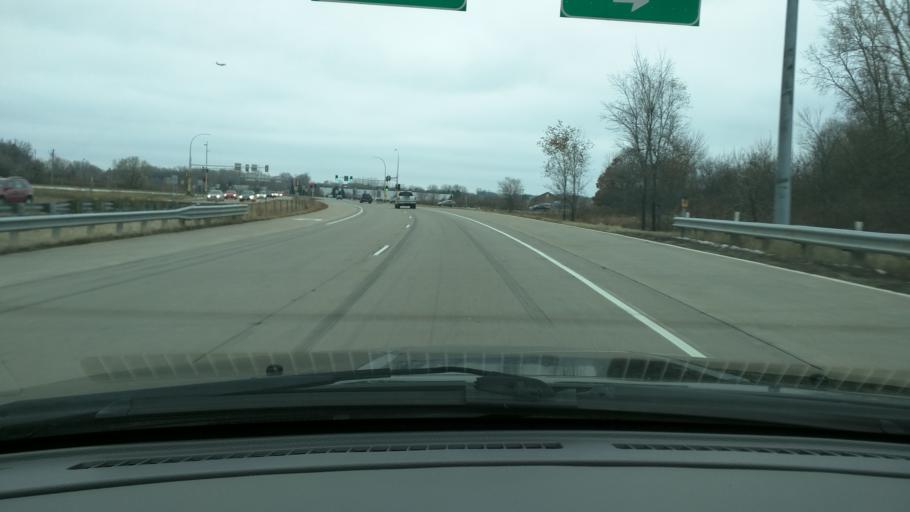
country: US
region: Minnesota
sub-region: Dakota County
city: Mendota Heights
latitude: 44.8753
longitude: -93.1640
